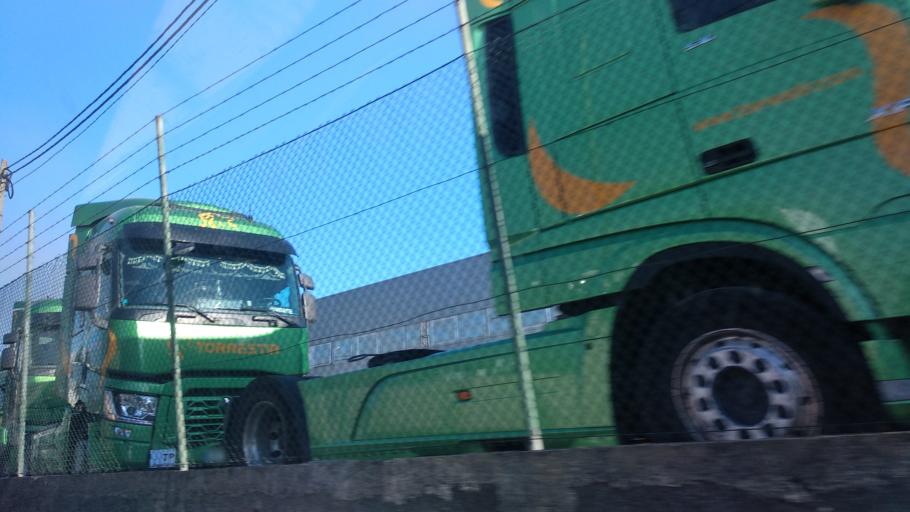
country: PT
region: Braga
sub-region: Braga
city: Braga
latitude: 41.5318
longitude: -8.4230
